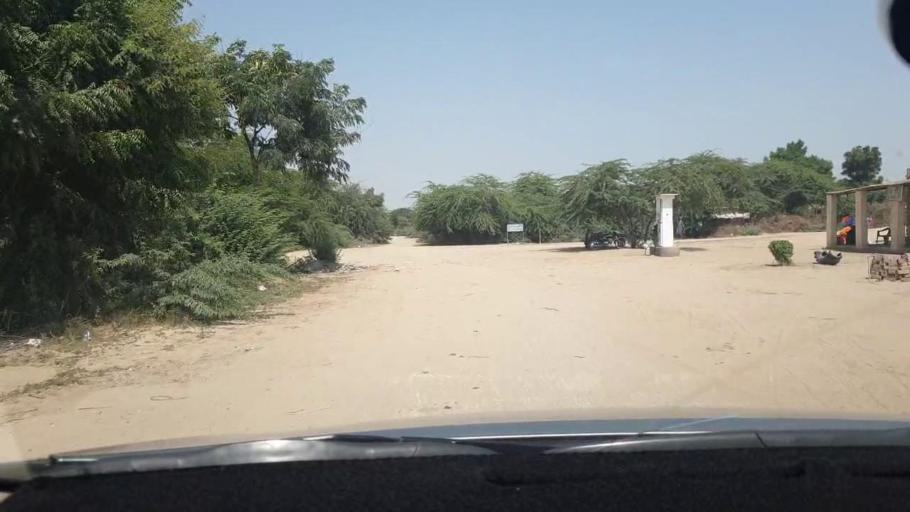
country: PK
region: Sindh
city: Tando Mittha Khan
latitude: 25.8520
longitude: 69.4245
